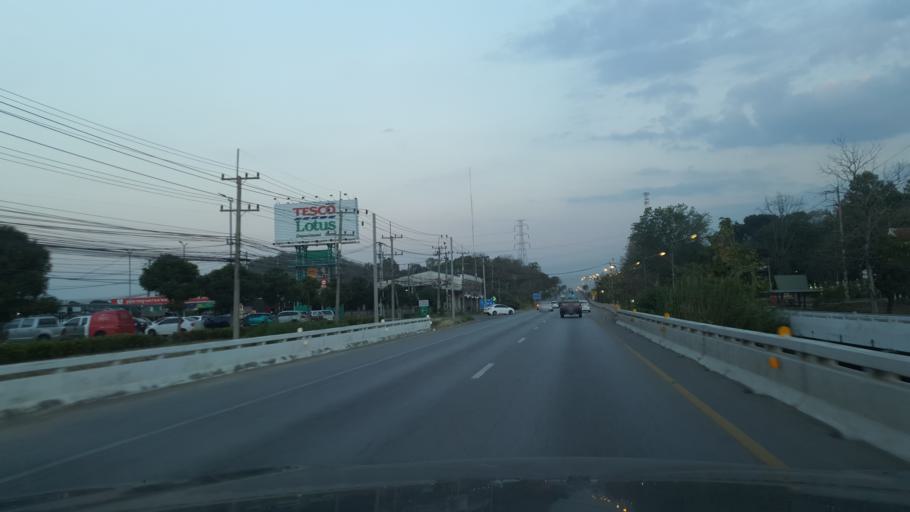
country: TH
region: Nakhon Sawan
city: Nakhon Sawan
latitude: 15.7072
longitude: 100.0948
